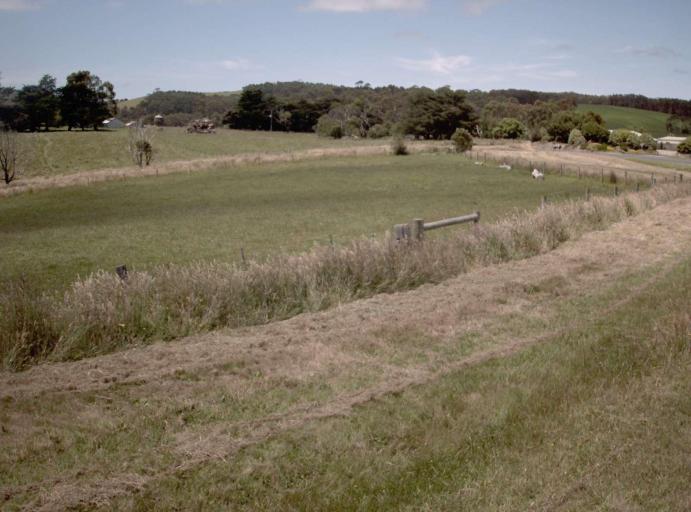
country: AU
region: Victoria
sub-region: Bass Coast
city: North Wonthaggi
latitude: -38.7142
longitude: 146.0994
